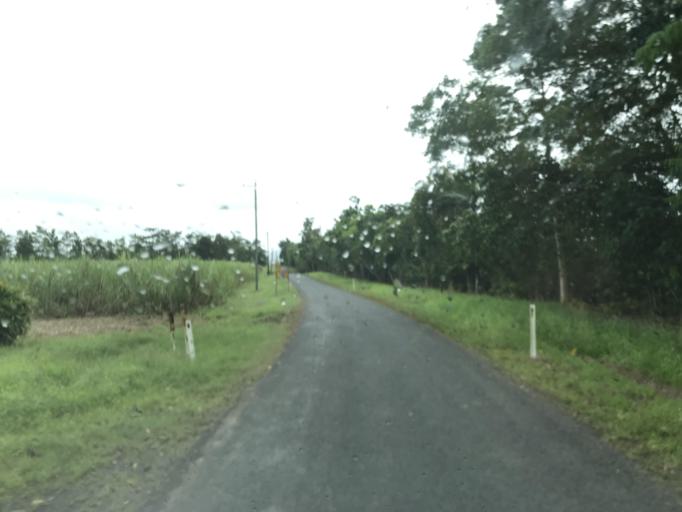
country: AU
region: Queensland
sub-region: Cassowary Coast
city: Innisfail
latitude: -17.4886
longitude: 145.9886
